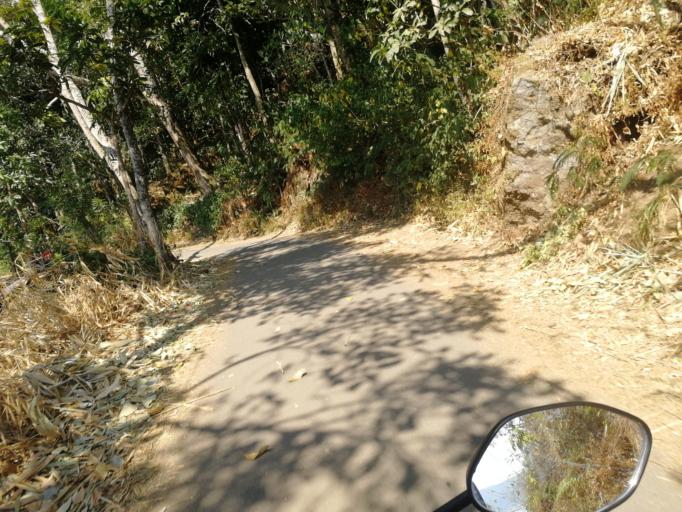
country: ID
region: Bali
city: Banjar Trunyan
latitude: -8.2610
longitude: 115.4229
